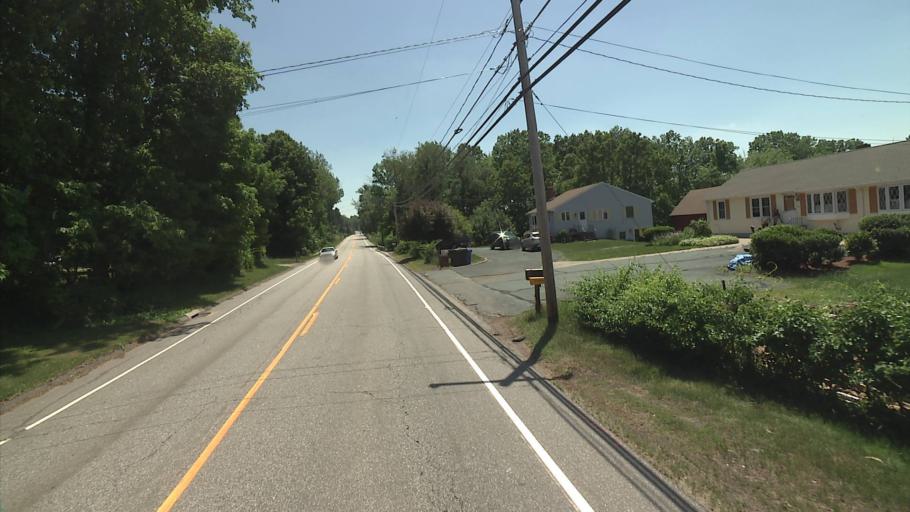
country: US
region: Connecticut
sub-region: Tolland County
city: Tolland
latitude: 41.8785
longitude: -72.4050
